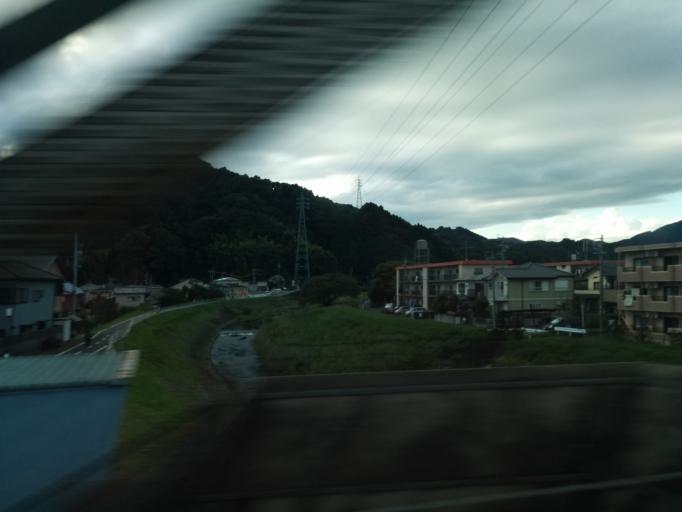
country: JP
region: Shizuoka
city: Shizuoka-shi
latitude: 34.9371
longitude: 138.3629
